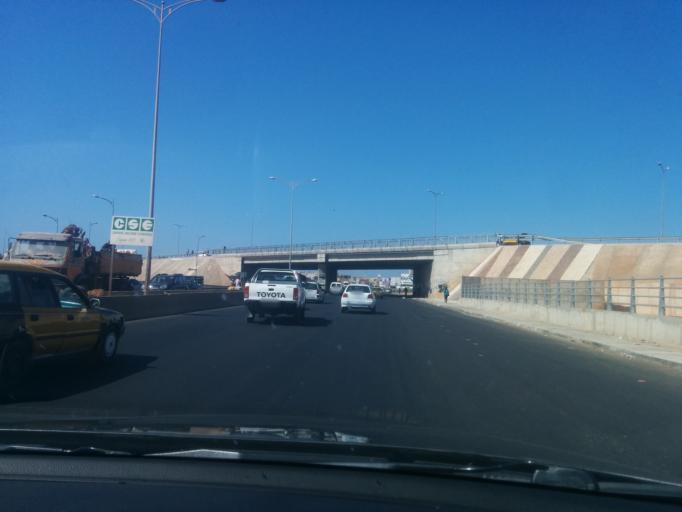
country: SN
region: Dakar
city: Grand Dakar
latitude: 14.7438
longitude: -17.4469
